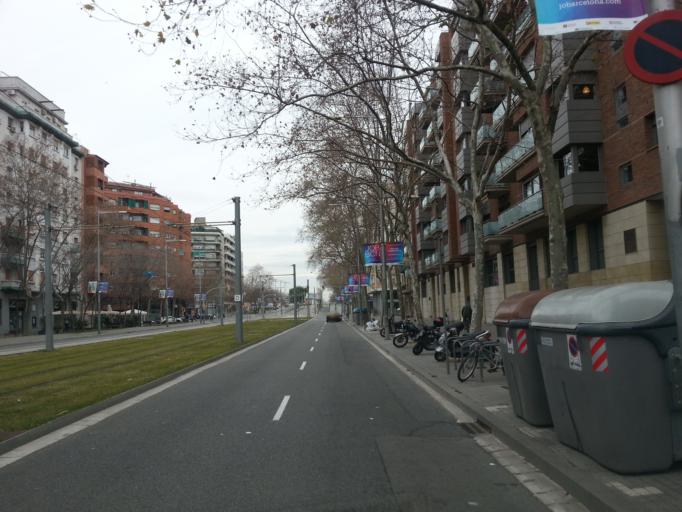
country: ES
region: Catalonia
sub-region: Provincia de Barcelona
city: Ciutat Vella
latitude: 41.3919
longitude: 2.1870
